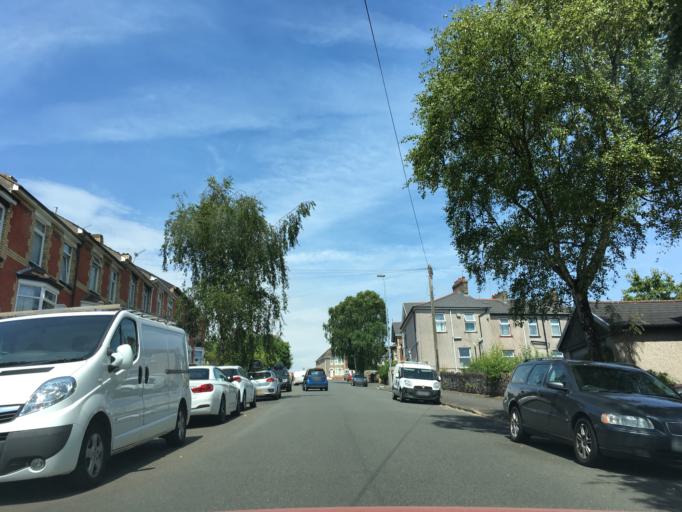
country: GB
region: Wales
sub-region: Newport
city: Newport
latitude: 51.5932
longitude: -2.9747
